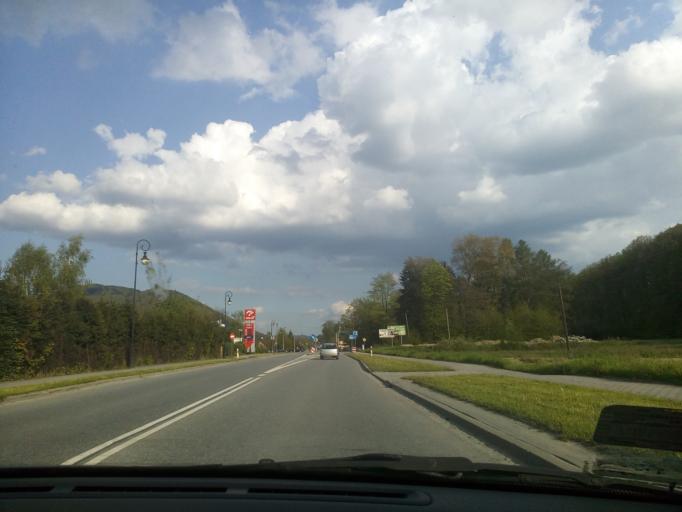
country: PL
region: Lesser Poland Voivodeship
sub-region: Powiat nowosadecki
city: Nawojowa
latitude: 49.5573
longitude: 20.7495
